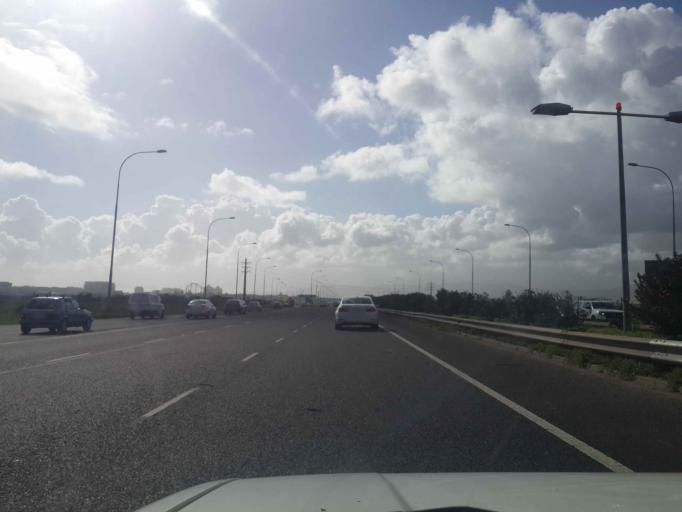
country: ZA
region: Western Cape
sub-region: City of Cape Town
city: Rosebank
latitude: -33.9093
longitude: 18.5005
